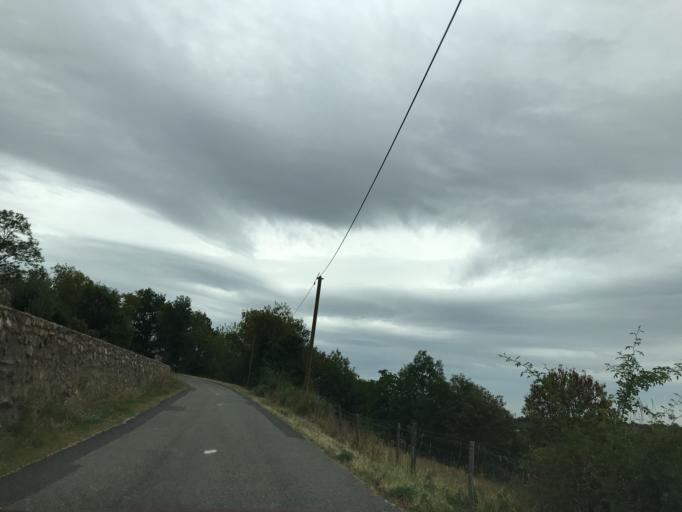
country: FR
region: Rhone-Alpes
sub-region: Departement de la Loire
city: Sail-sous-Couzan
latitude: 45.6940
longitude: 3.9257
